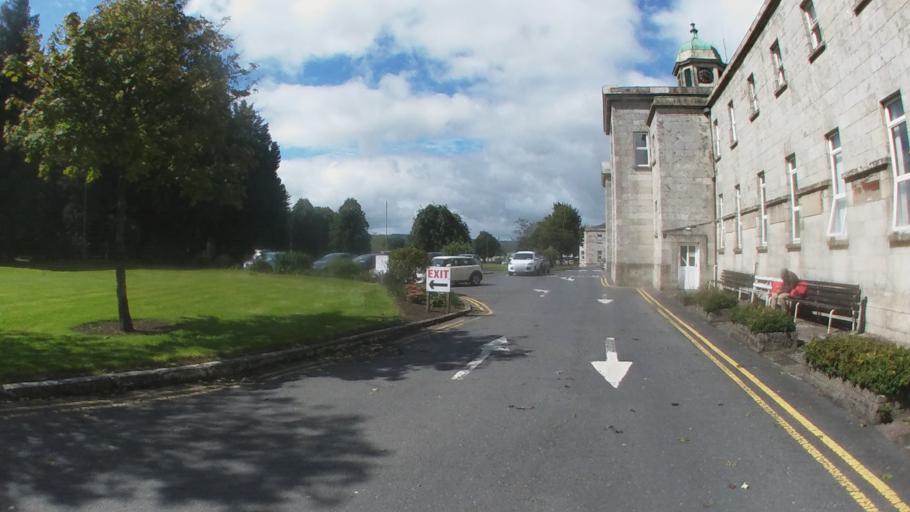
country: IE
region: Leinster
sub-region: County Carlow
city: Carlow
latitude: 52.8421
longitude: -6.9266
